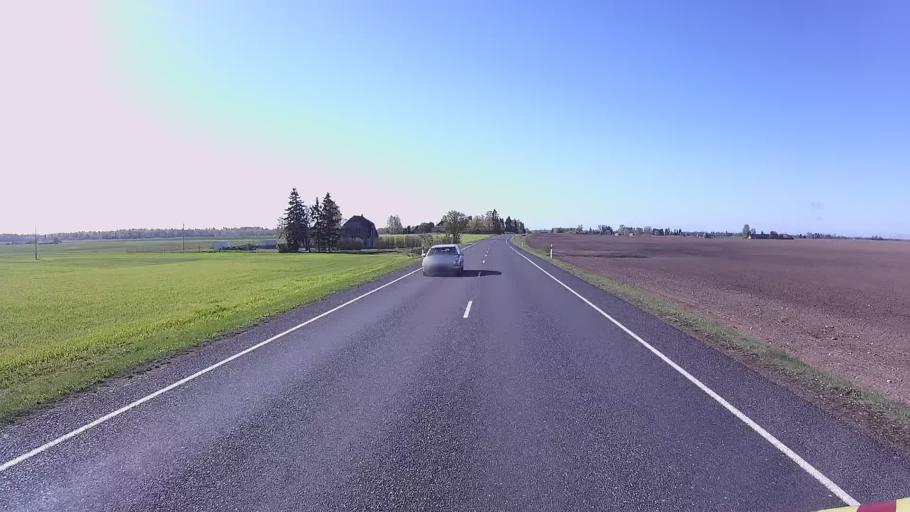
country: EE
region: Viljandimaa
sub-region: Vohma linn
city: Vohma
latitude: 58.6713
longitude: 25.6061
